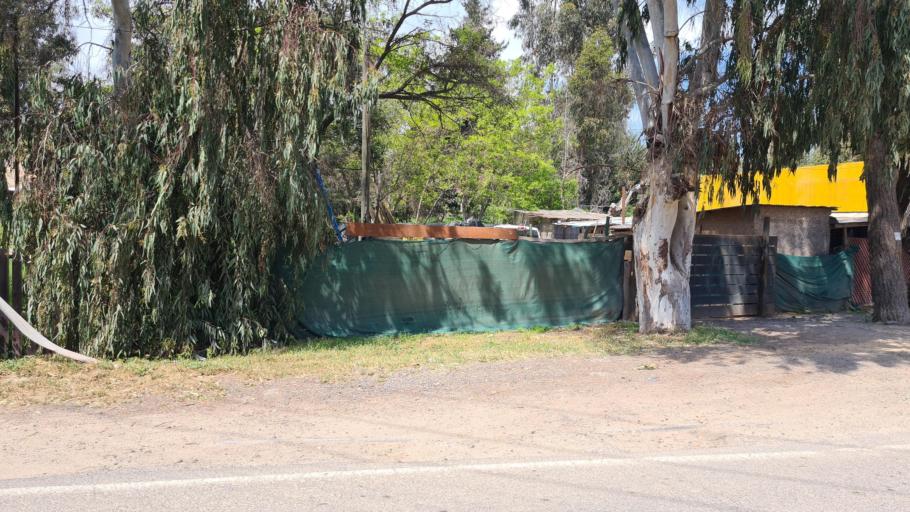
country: CL
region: O'Higgins
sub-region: Provincia de Cachapoal
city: San Vicente
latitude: -34.1510
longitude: -71.4594
